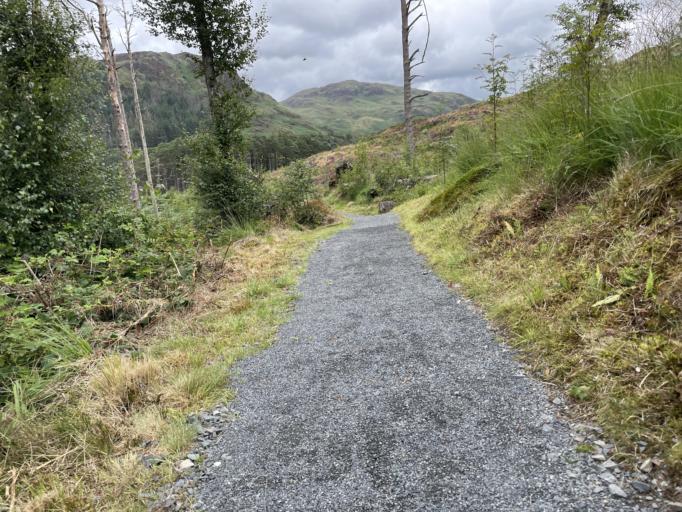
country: GB
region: Scotland
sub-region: Dumfries and Galloway
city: Newton Stewart
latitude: 55.0853
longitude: -4.4956
